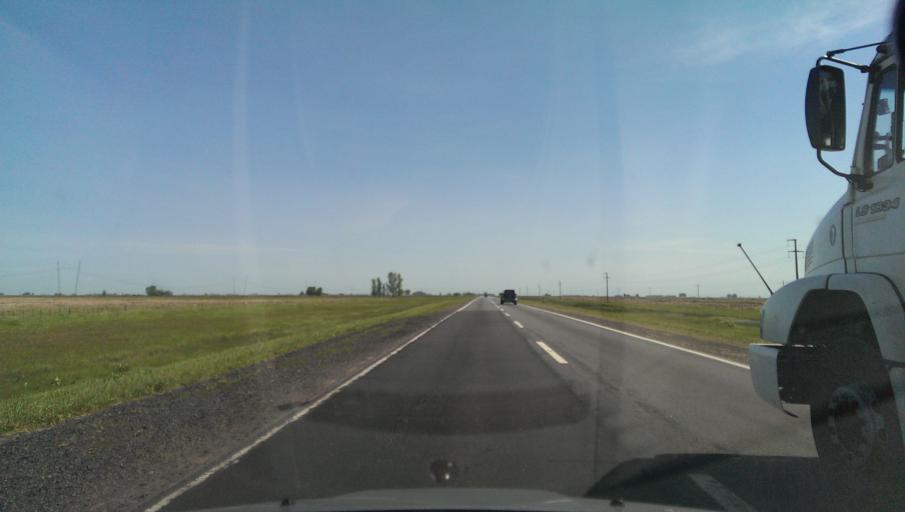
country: AR
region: Buenos Aires
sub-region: Partido de Azul
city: Azul
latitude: -36.6212
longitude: -59.6897
